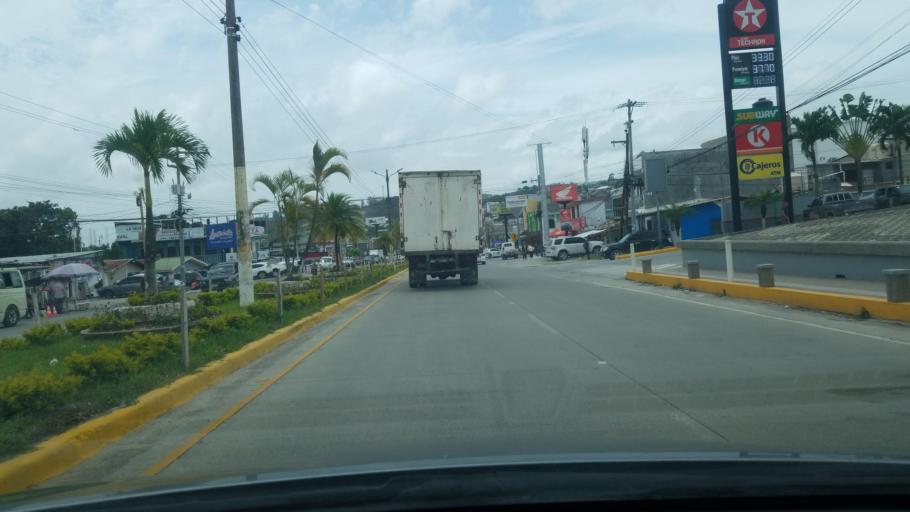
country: HN
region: Copan
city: Santa Rosa de Copan
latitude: 14.7773
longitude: -88.7785
